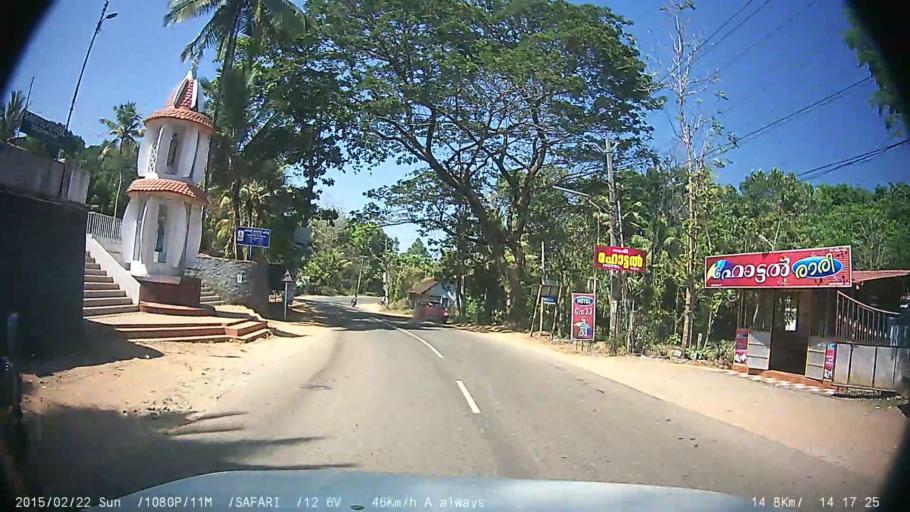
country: IN
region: Kerala
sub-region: Kottayam
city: Lalam
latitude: 9.5616
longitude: 76.6823
